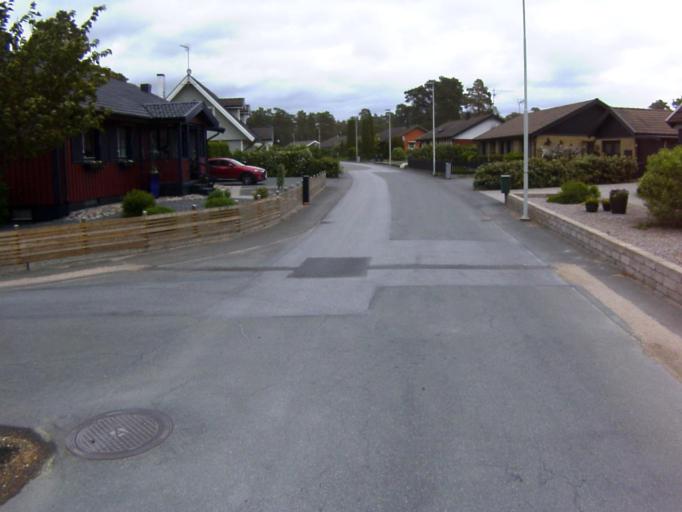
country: SE
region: Skane
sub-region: Kristianstads Kommun
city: Ahus
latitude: 55.9413
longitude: 14.2753
